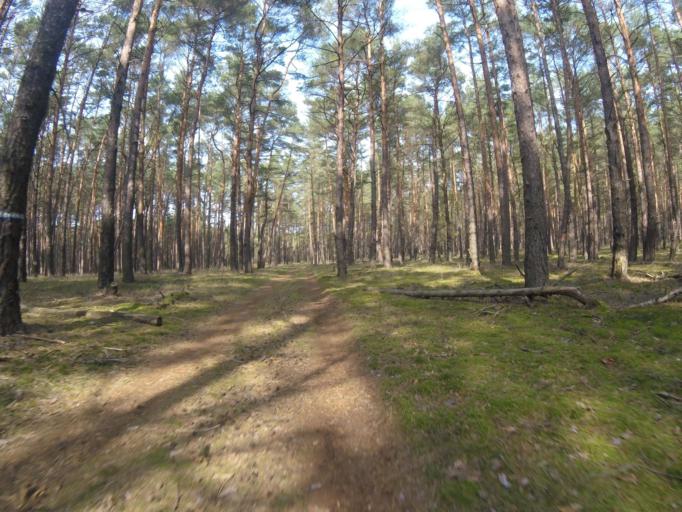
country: DE
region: Brandenburg
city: Bestensee
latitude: 52.2546
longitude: 13.6841
